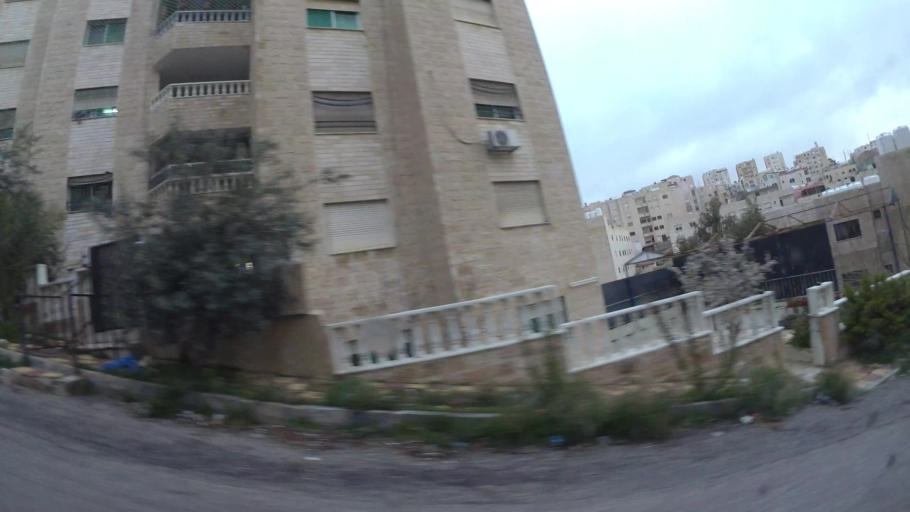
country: JO
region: Amman
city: Amman
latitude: 32.0030
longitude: 35.9329
